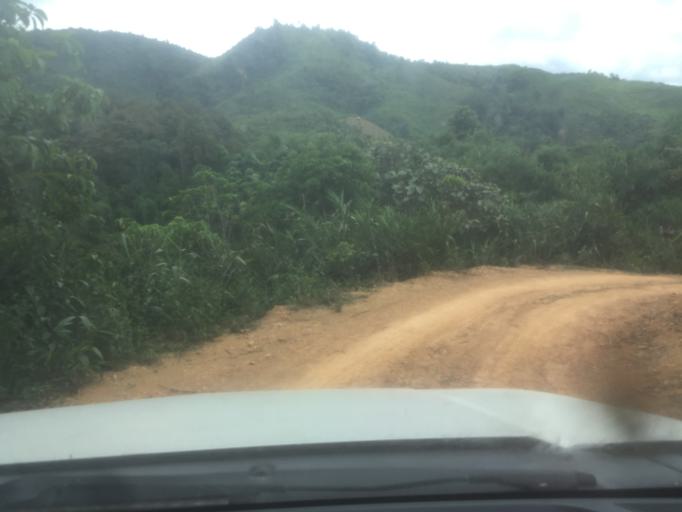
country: LA
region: Phongsali
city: Khoa
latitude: 20.9147
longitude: 102.5608
